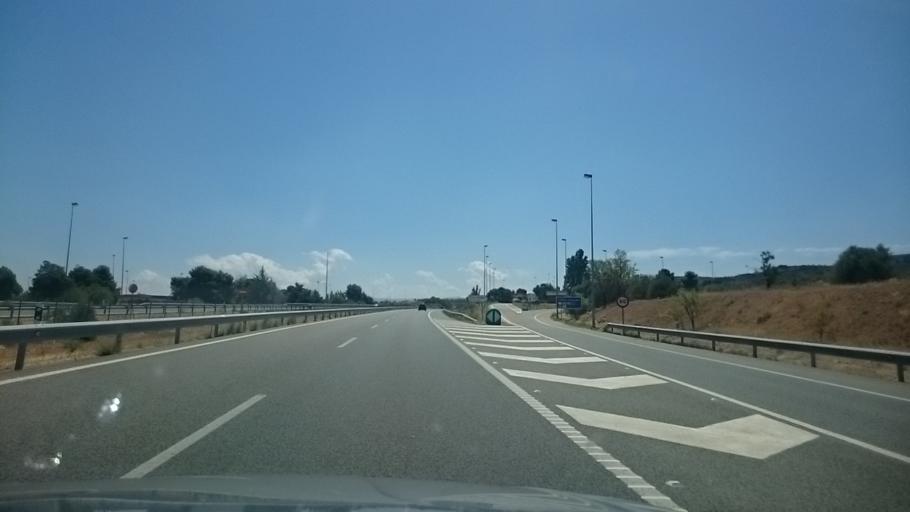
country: ES
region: Catalonia
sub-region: Provincia de Lleida
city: Juneda
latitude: 41.4907
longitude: 0.8629
